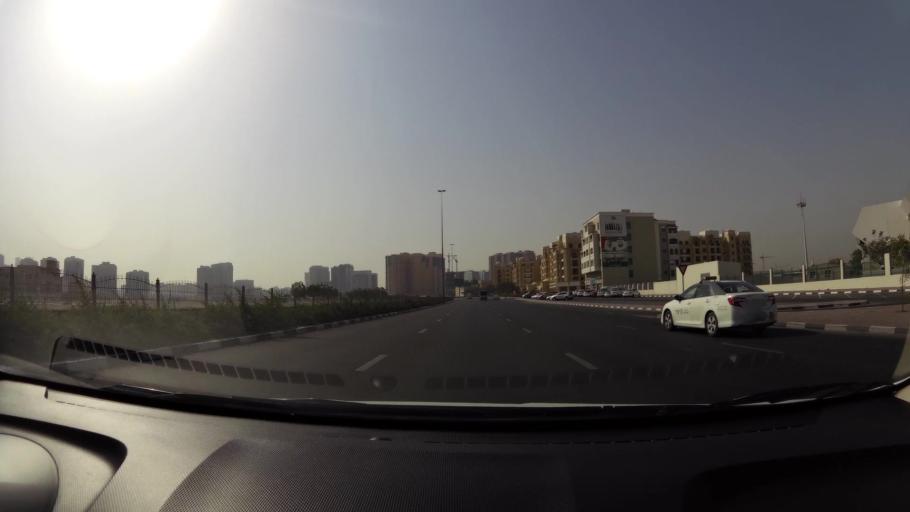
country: AE
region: Ash Shariqah
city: Sharjah
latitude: 25.2927
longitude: 55.3519
